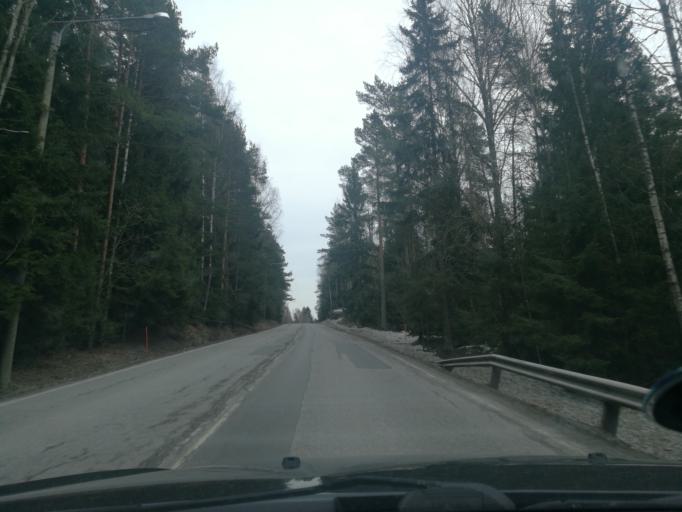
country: FI
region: Uusimaa
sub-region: Helsinki
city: Nickby
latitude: 60.2783
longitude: 25.3761
